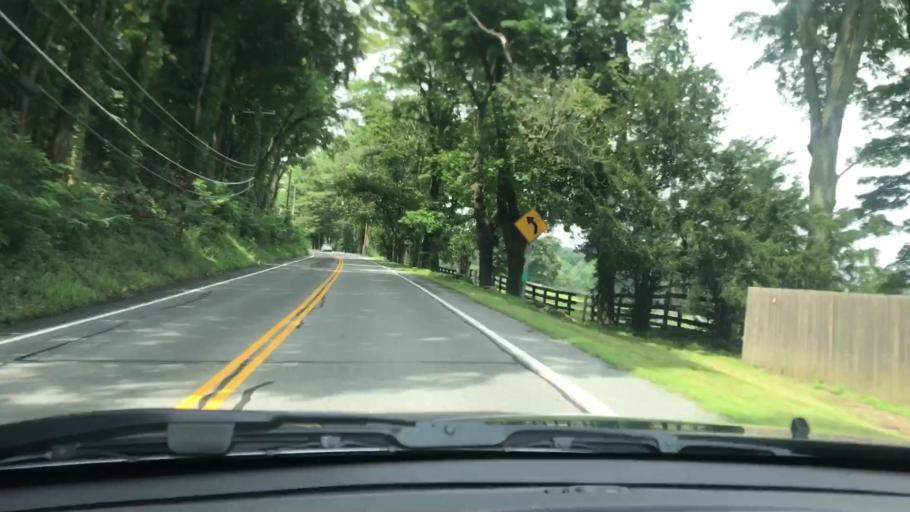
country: US
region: New York
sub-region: Westchester County
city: Bedford
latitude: 41.1966
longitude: -73.6628
